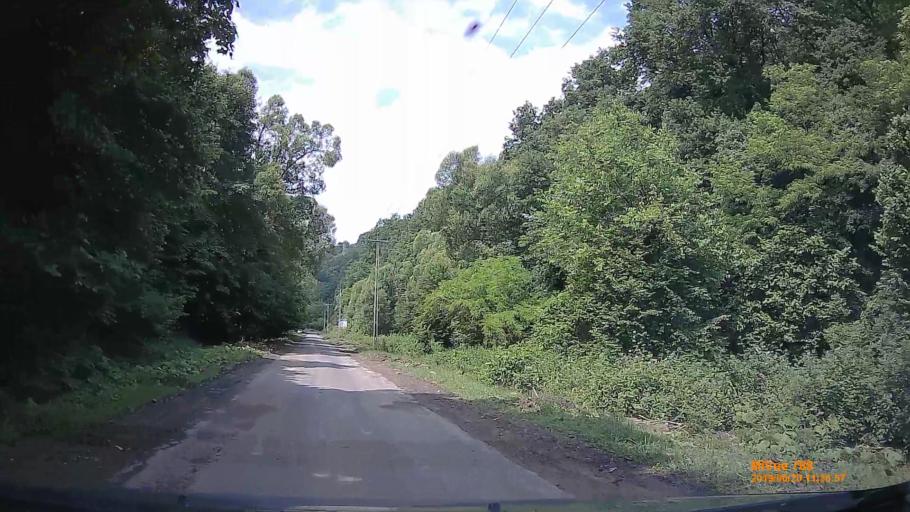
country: HU
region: Baranya
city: Mecseknadasd
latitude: 46.2250
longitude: 18.4343
